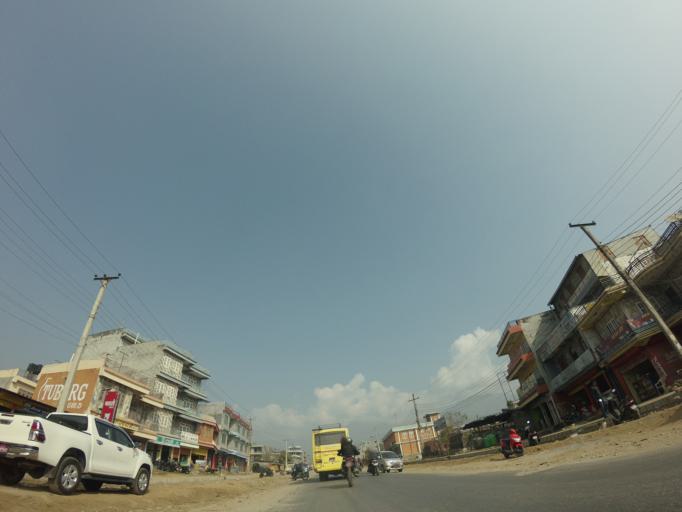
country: NP
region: Western Region
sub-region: Gandaki Zone
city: Pokhara
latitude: 28.2332
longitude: 83.9828
